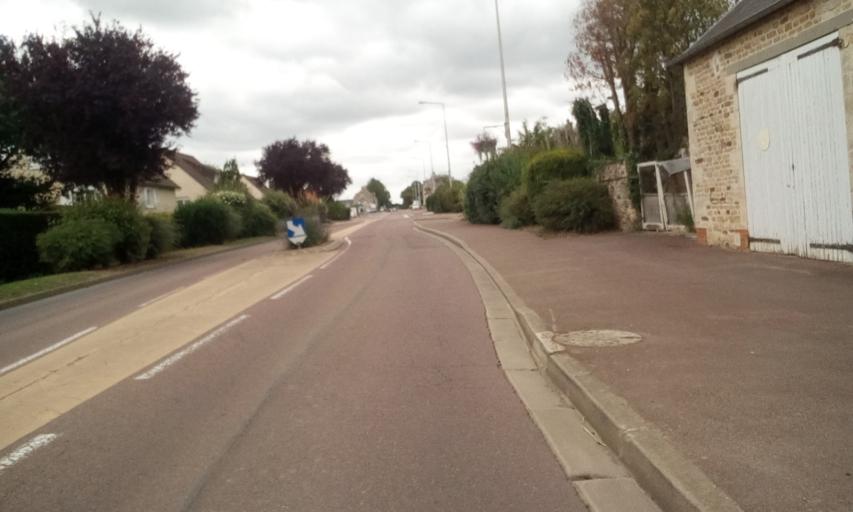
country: FR
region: Lower Normandy
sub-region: Departement du Calvados
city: Tourville-sur-Odon
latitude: 49.1402
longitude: -0.5056
